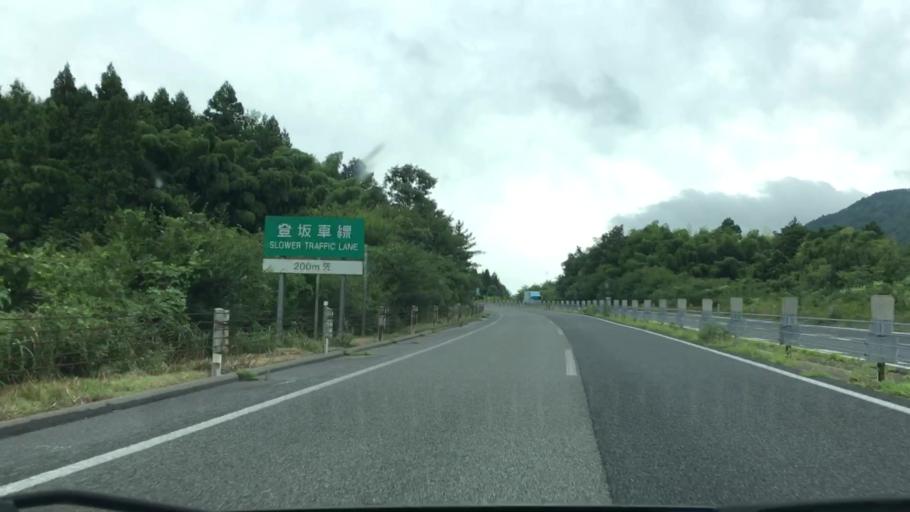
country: JP
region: Hiroshima
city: Hiroshima-shi
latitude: 34.6399
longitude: 132.5155
